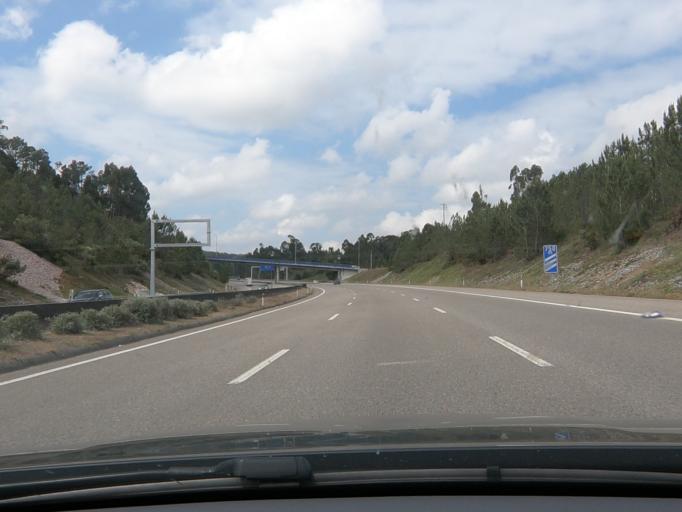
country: PT
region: Leiria
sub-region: Leiria
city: Maceira
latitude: 39.7203
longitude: -8.9098
